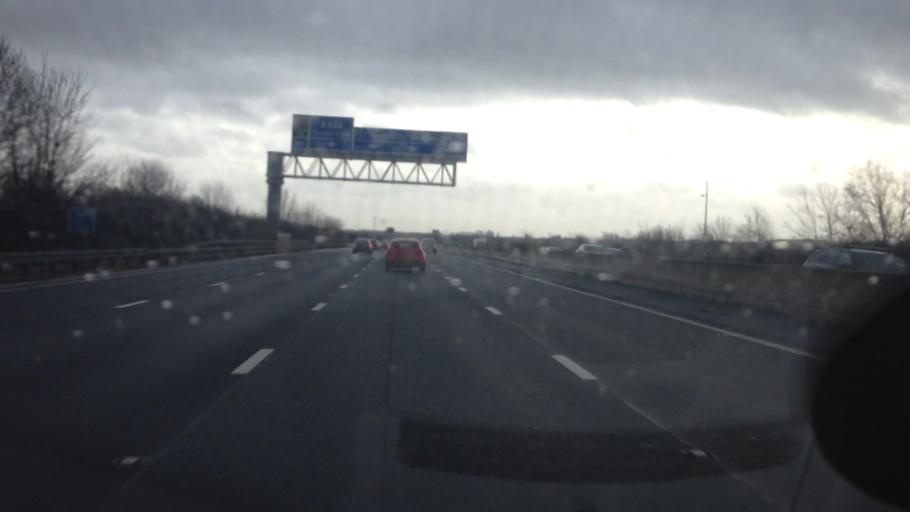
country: GB
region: England
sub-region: City and Borough of Wakefield
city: Crigglestone
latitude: 53.6628
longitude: -1.5354
